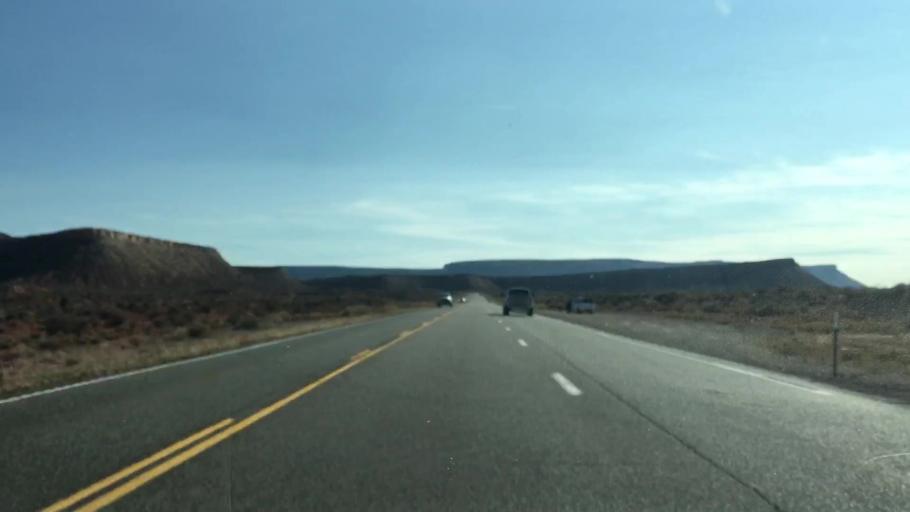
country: US
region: Utah
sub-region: Washington County
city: Hurricane
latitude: 37.1547
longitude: -113.2585
